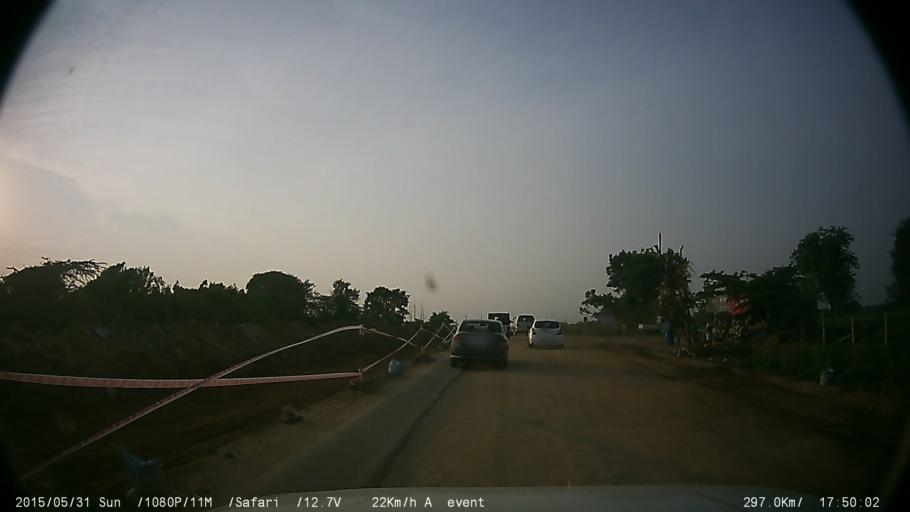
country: IN
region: Karnataka
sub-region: Mysore
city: Nanjangud
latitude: 11.9730
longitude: 76.6697
